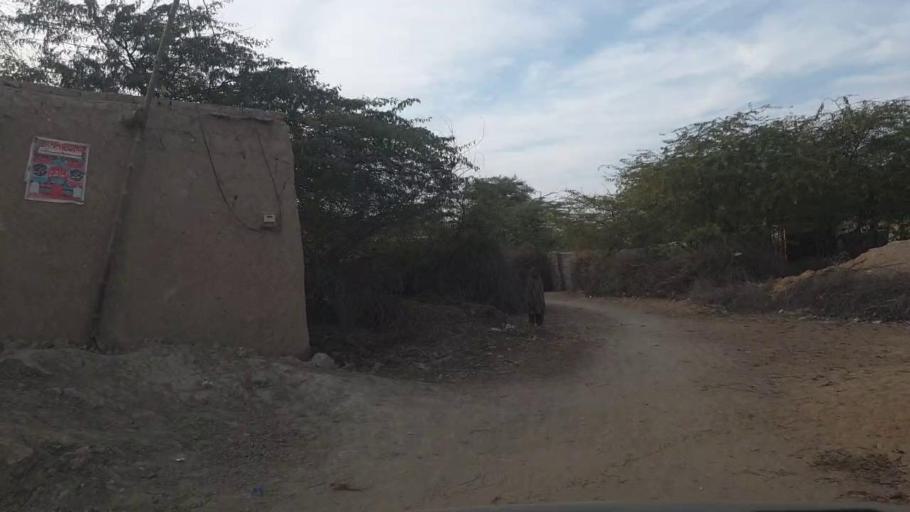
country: PK
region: Sindh
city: Shahpur Chakar
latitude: 26.1225
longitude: 68.5907
